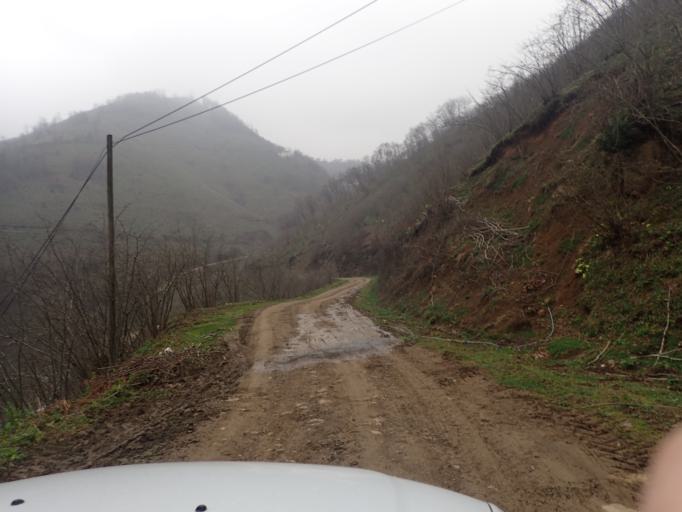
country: TR
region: Ordu
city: Camas
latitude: 40.8988
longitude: 37.5557
